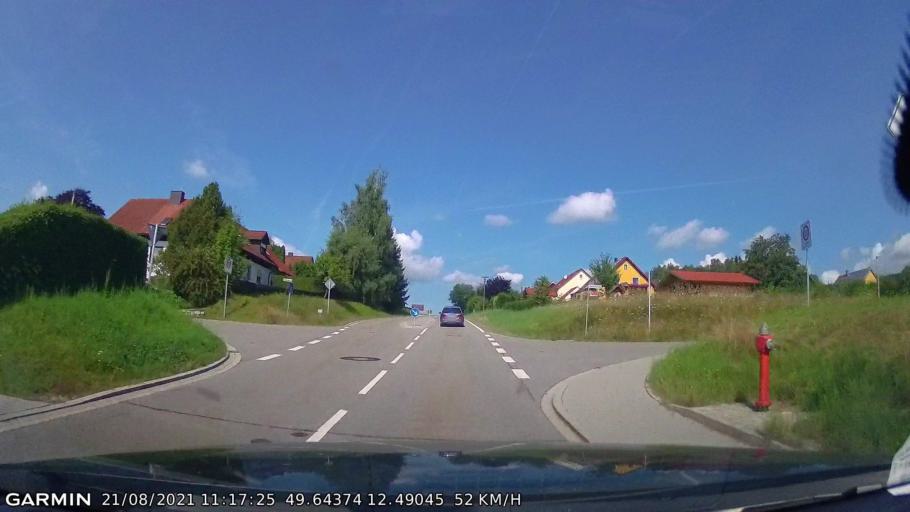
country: DE
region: Bavaria
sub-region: Upper Palatinate
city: Waidhaus
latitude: 49.6438
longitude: 12.4904
